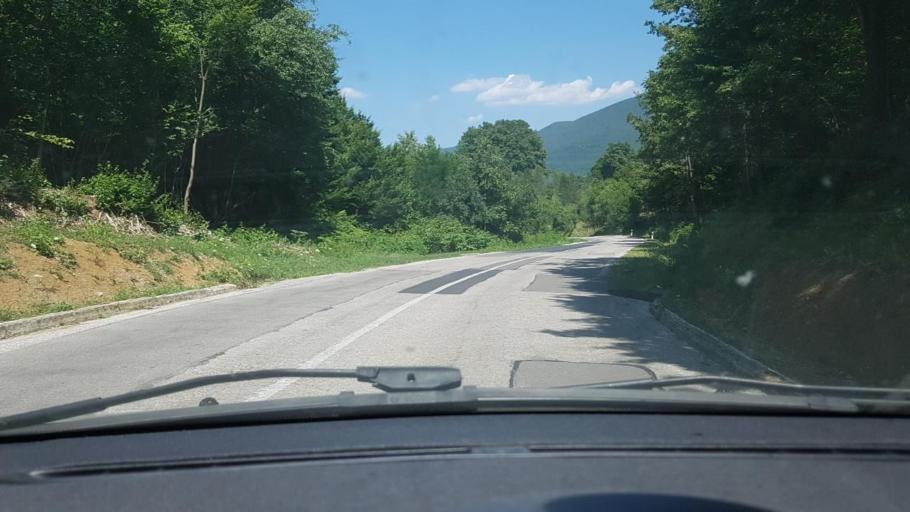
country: BA
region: Federation of Bosnia and Herzegovina
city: Orasac
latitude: 44.6135
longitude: 16.0696
